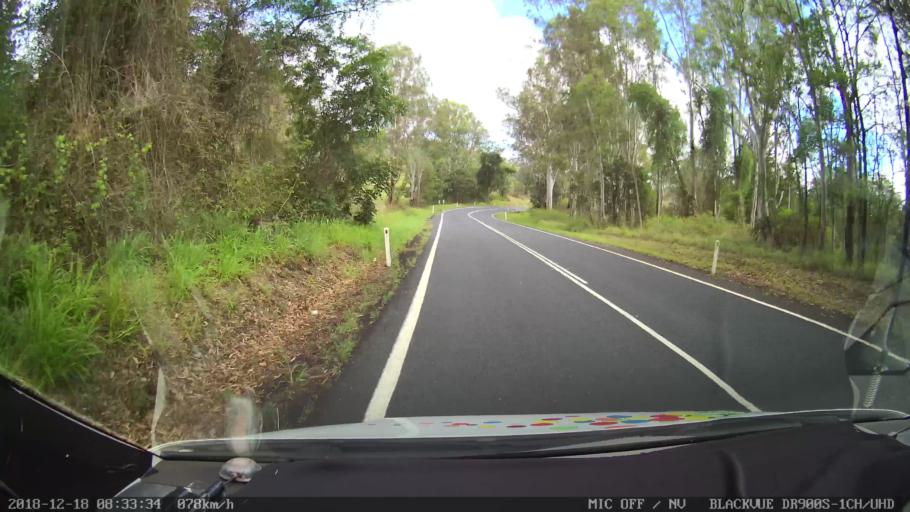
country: AU
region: New South Wales
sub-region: Kyogle
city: Kyogle
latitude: -28.2899
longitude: 152.7861
